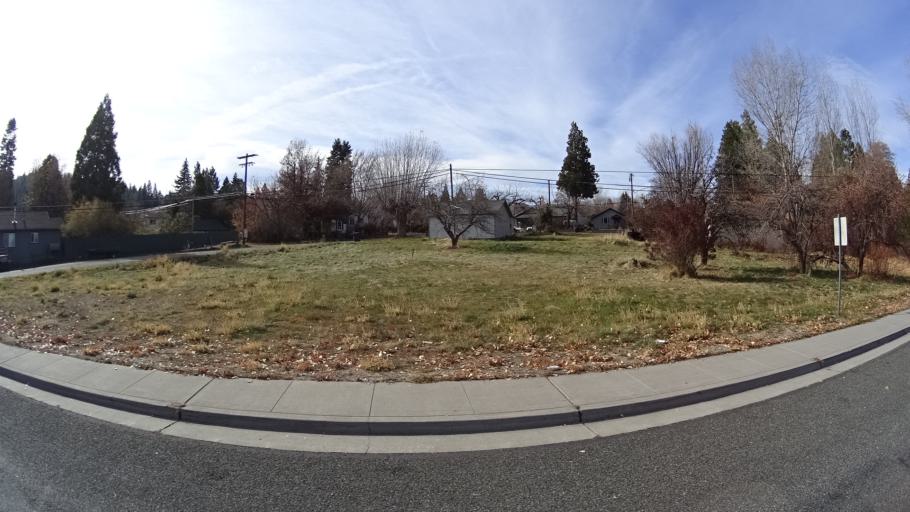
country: US
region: California
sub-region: Siskiyou County
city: Weed
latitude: 41.4158
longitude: -122.3841
